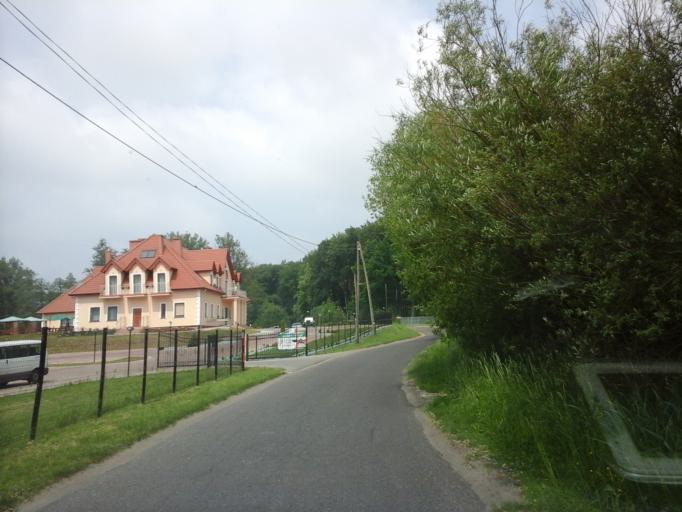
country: PL
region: West Pomeranian Voivodeship
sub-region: Powiat mysliborski
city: Barlinek
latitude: 53.0098
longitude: 15.2246
